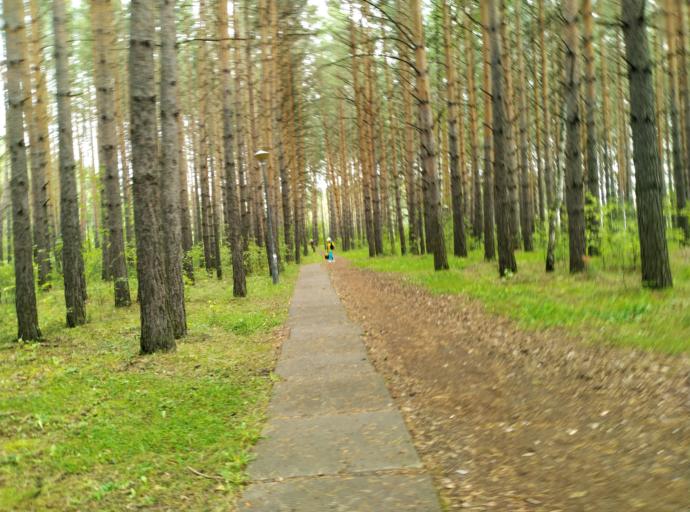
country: RU
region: Krasnoyarskiy
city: Krasnoyarsk
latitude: 55.9918
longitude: 92.7619
